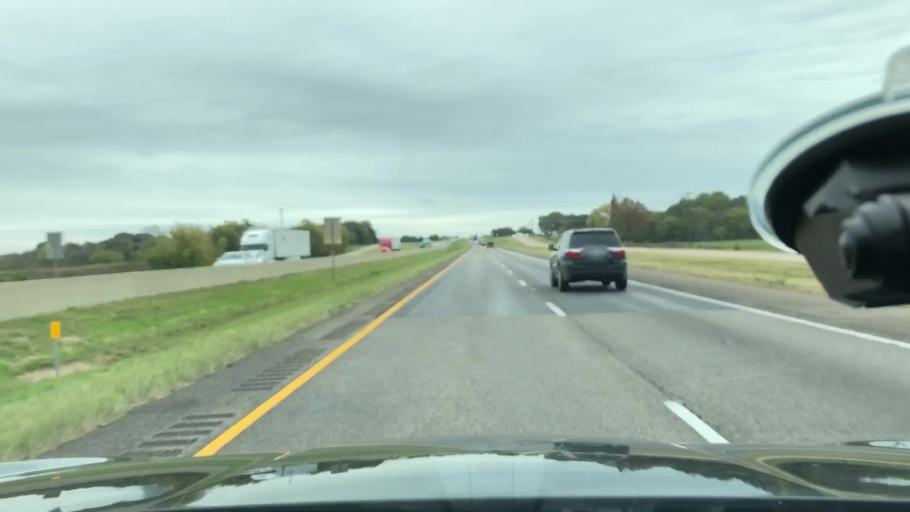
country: US
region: Texas
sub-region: Hopkins County
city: Sulphur Springs
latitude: 33.1513
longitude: -95.4380
